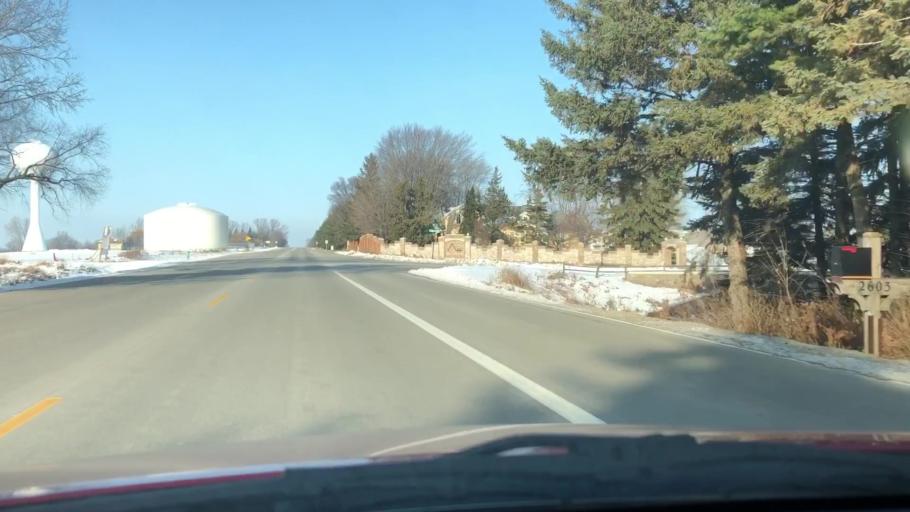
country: US
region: Wisconsin
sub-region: Outagamie County
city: Kimberly
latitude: 44.3327
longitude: -88.3750
